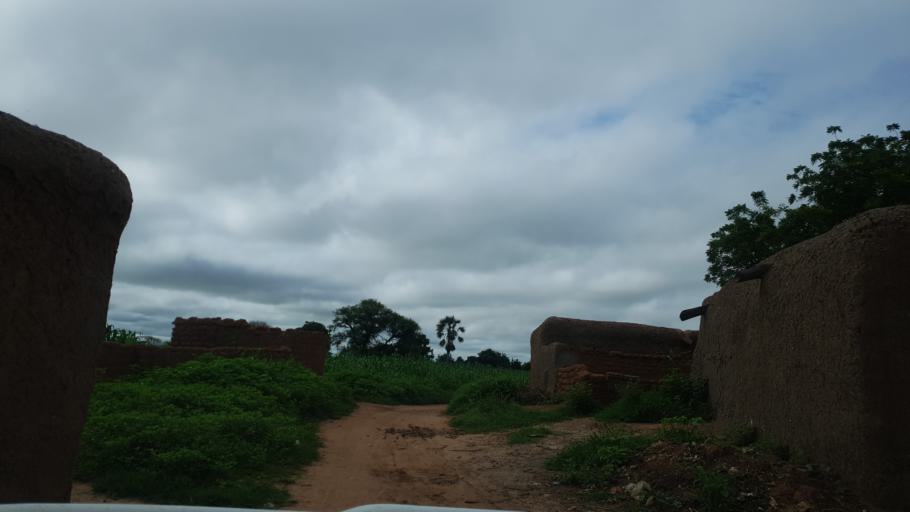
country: ML
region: Segou
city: Baroueli
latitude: 13.5044
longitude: -6.8983
